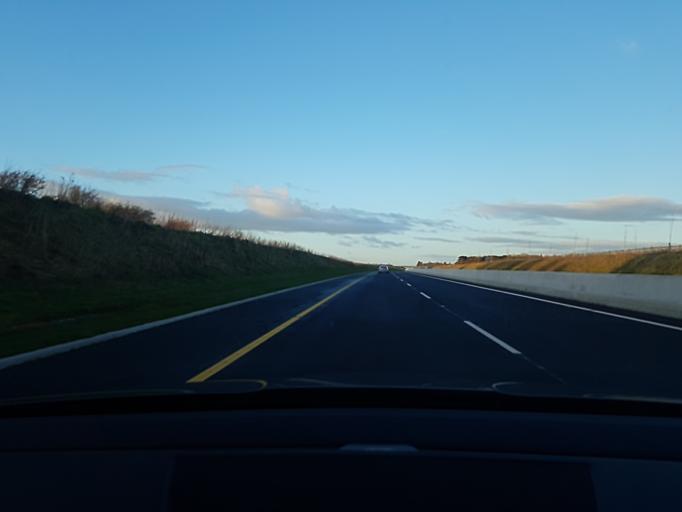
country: IE
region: Connaught
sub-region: County Galway
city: Athenry
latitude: 53.3291
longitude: -8.8033
